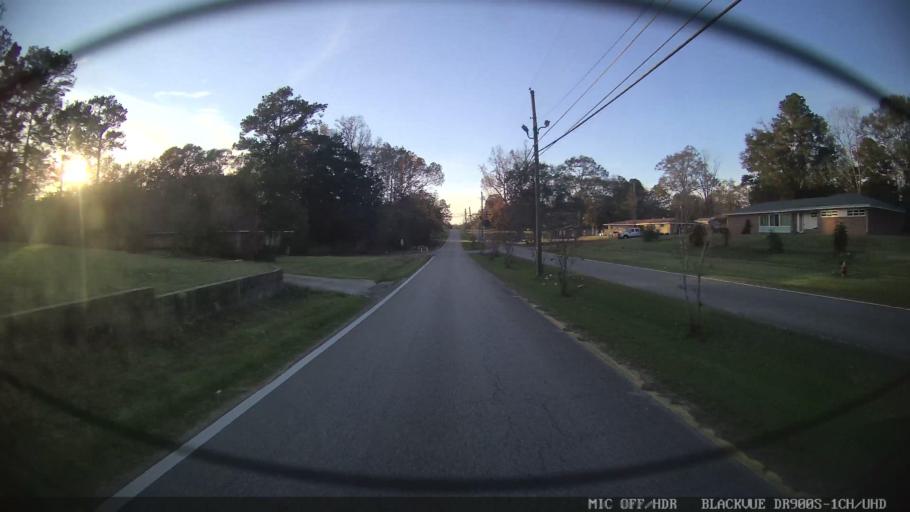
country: US
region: Mississippi
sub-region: Lamar County
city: Lumberton
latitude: 31.0027
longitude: -89.4558
